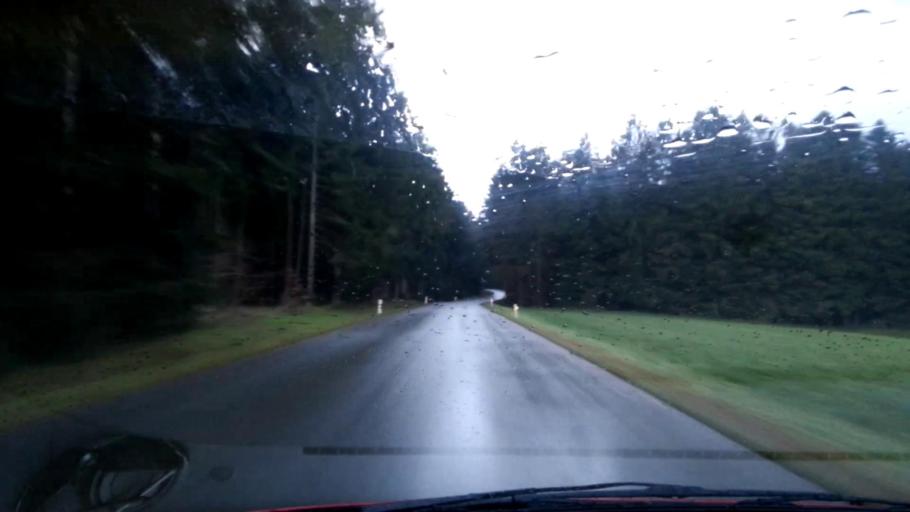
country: DE
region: Bavaria
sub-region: Upper Franconia
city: Aufsess
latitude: 49.9364
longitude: 11.2434
